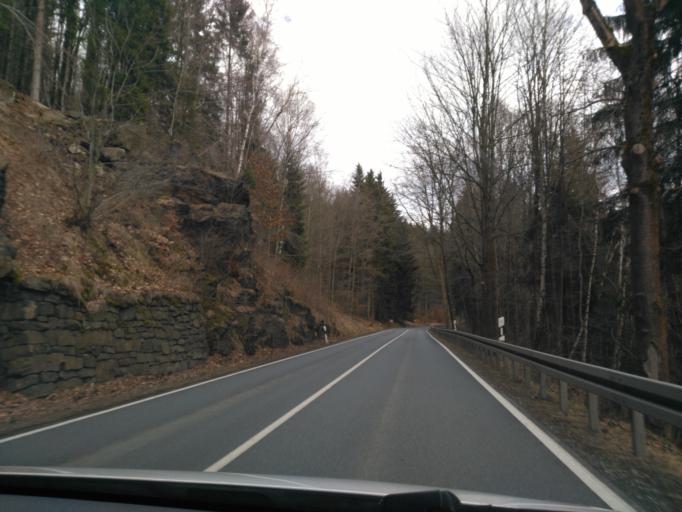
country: DE
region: Saxony
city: Wolkenstein
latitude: 50.6611
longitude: 13.0580
